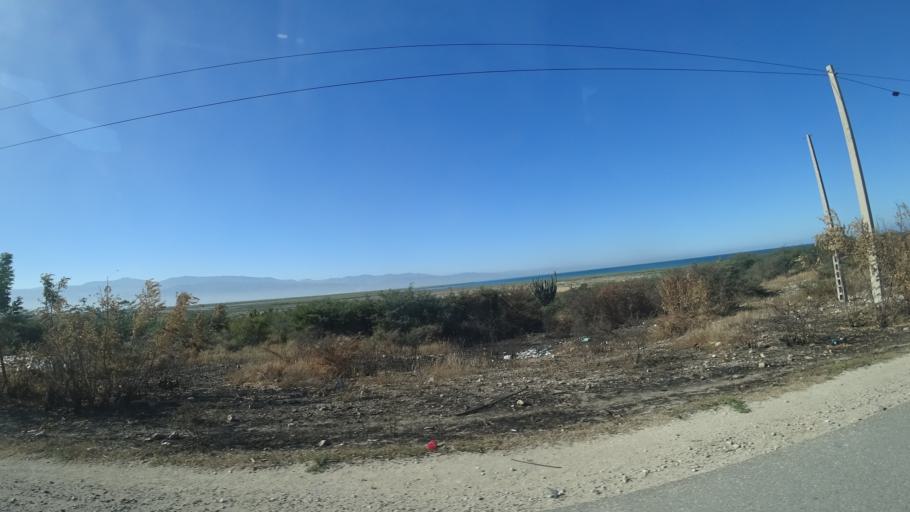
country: HT
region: Ouest
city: Cabaret
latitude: 18.6723
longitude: -72.3108
